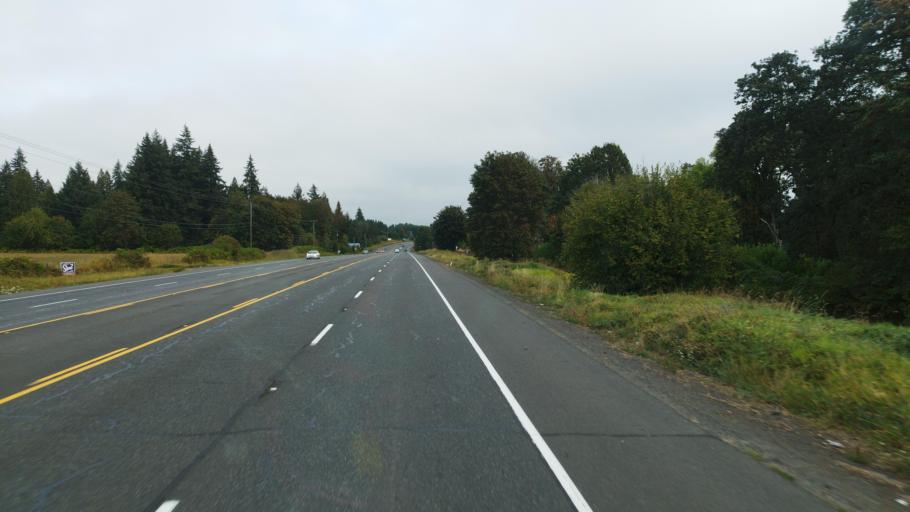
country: US
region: Oregon
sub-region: Columbia County
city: Warren
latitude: 45.7936
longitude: -122.8681
